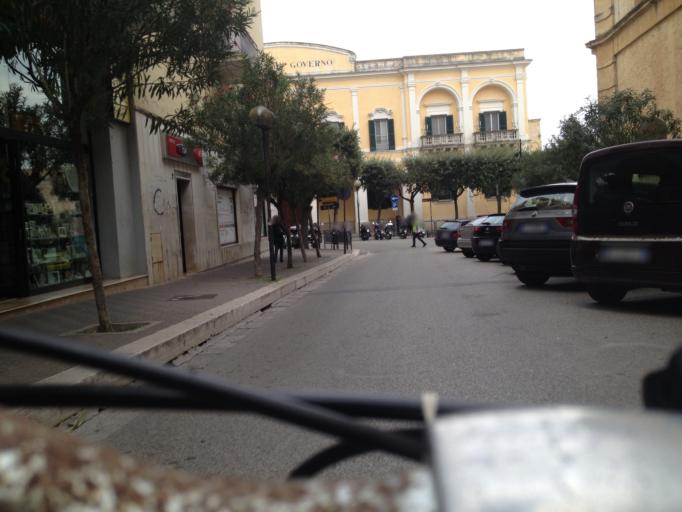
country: IT
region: Basilicate
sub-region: Provincia di Matera
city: Matera
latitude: 40.6673
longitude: 16.6055
